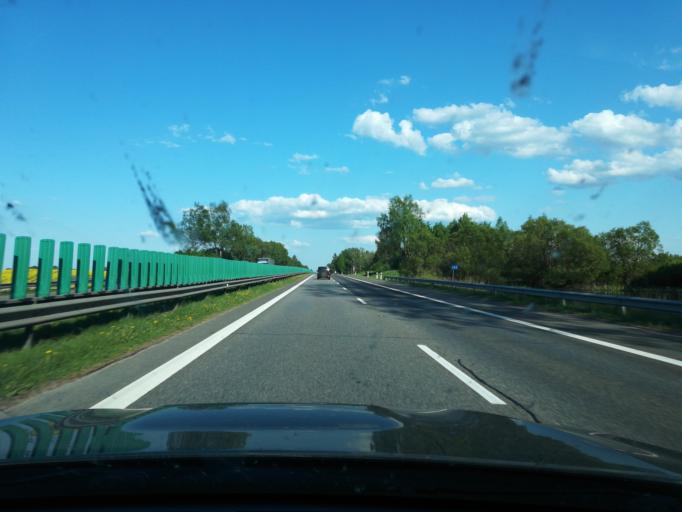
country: LT
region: Vilnius County
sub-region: Vilniaus Rajonas
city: Vievis
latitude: 54.7838
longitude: 24.7447
